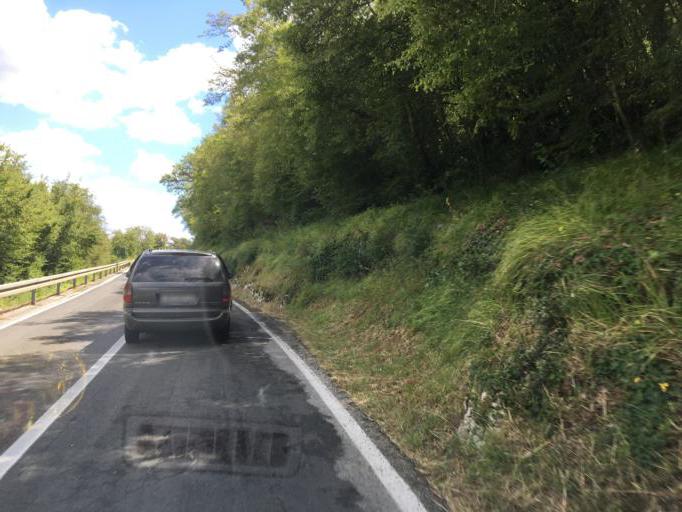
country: HR
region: Istarska
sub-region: Grad Rovinj
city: Rovinj
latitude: 45.1197
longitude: 13.7574
